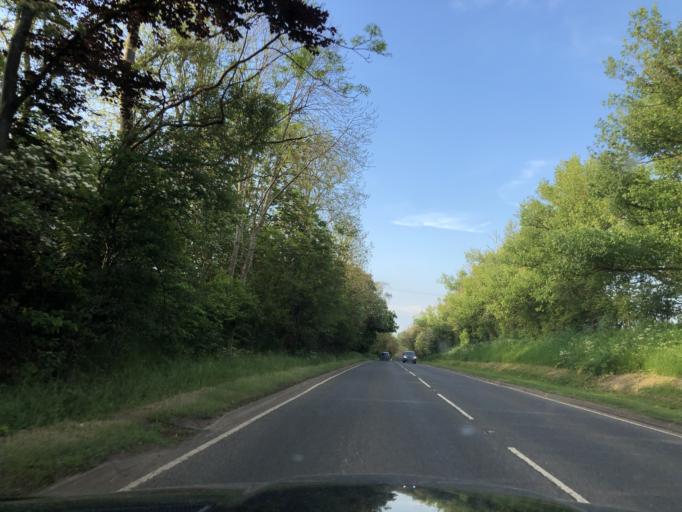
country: GB
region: England
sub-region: Warwickshire
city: Shipston on Stour
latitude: 52.1011
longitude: -1.6263
